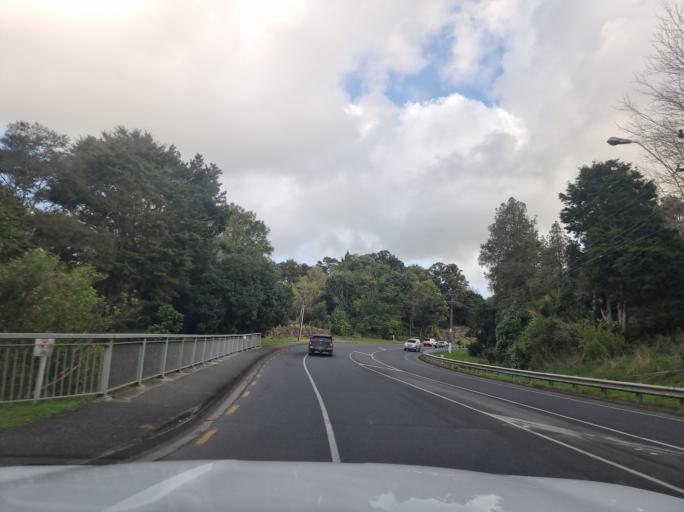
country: NZ
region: Northland
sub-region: Whangarei
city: Whangarei
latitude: -35.7364
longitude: 174.2853
